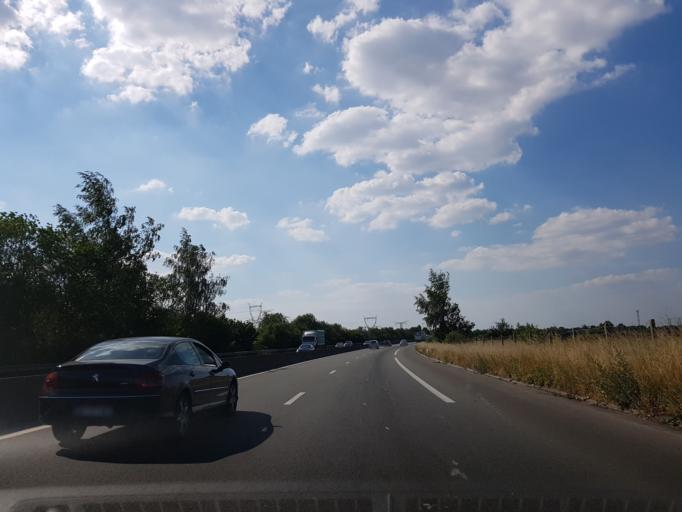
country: FR
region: Nord-Pas-de-Calais
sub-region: Departement du Nord
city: Somain
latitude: 50.3490
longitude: 3.2665
